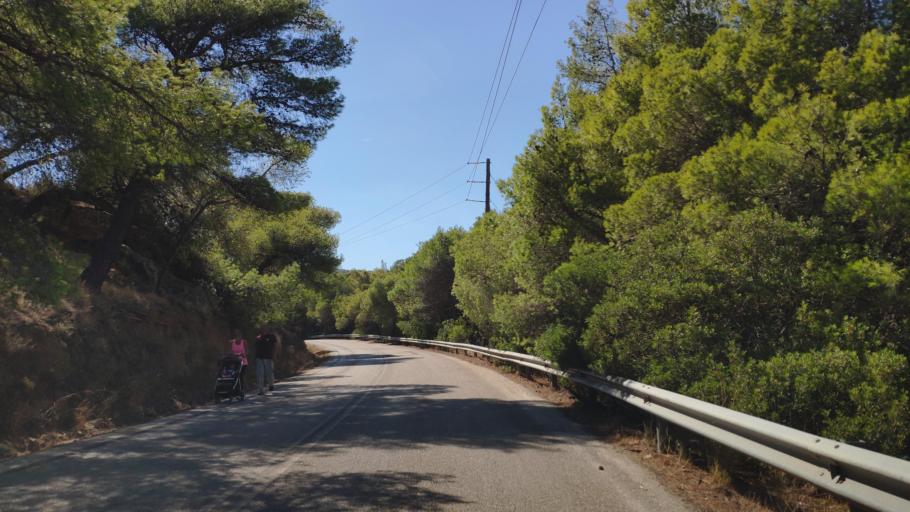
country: GR
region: Attica
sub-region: Nomarchia Anatolikis Attikis
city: Limin Mesoyaias
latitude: 37.8438
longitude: 24.0152
